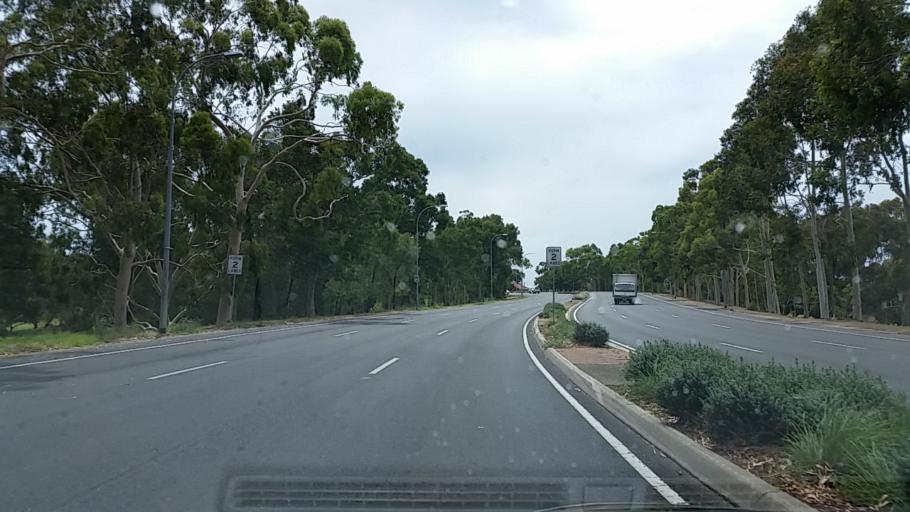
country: AU
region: South Australia
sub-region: Adelaide
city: North Adelaide
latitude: -34.9155
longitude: 138.5930
